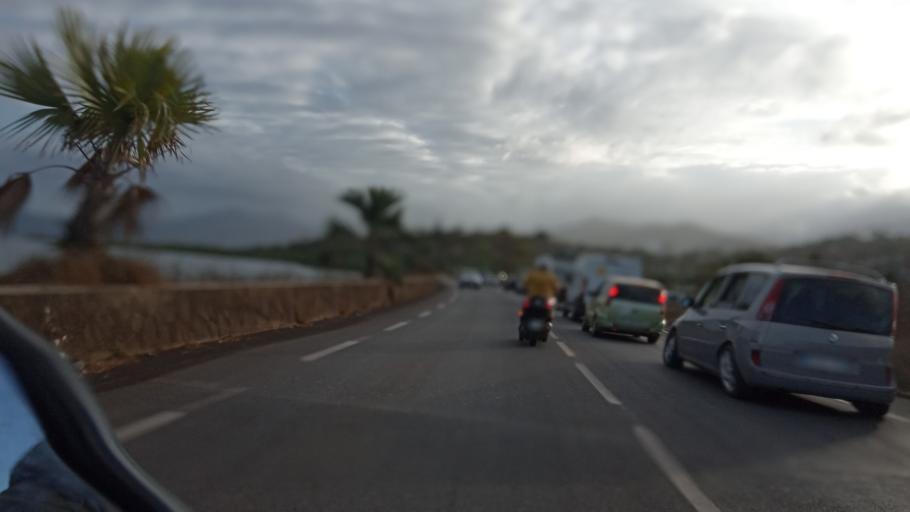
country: YT
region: Mamoudzou
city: Mamoudzou
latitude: -12.7936
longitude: 45.2192
